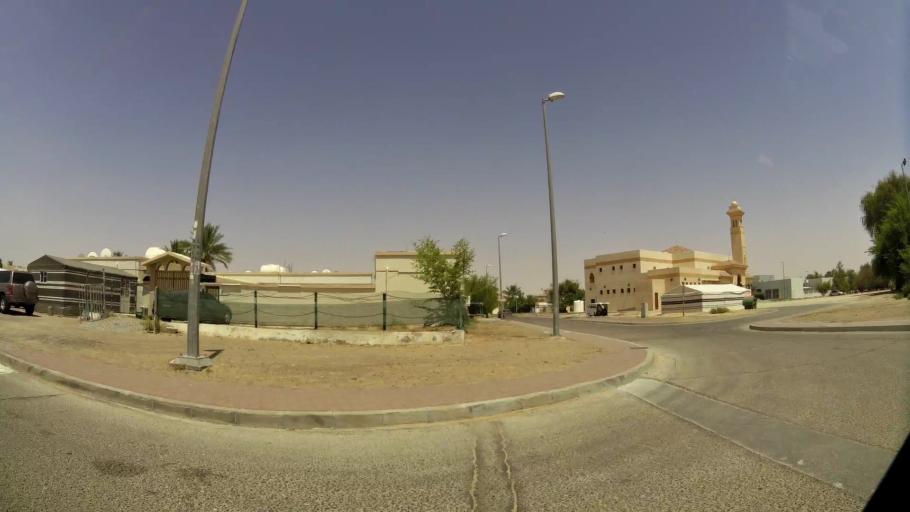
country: OM
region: Al Buraimi
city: Al Buraymi
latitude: 24.2864
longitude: 55.7650
